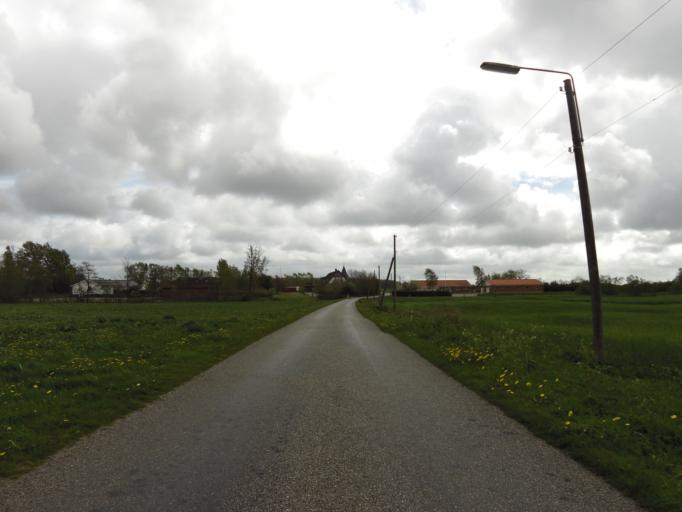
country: DK
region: South Denmark
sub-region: Tonder Kommune
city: Sherrebek
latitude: 55.2088
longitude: 8.8868
